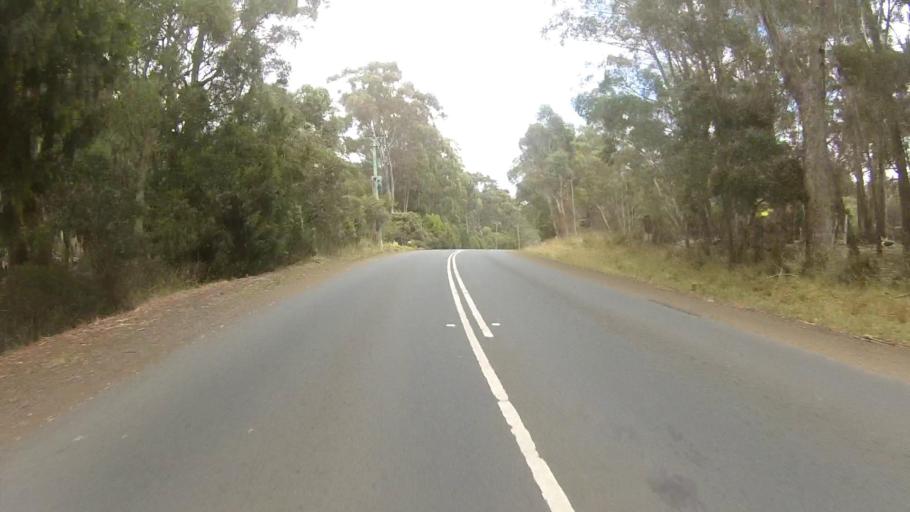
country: AU
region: Tasmania
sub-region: Kingborough
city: Margate
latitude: -42.9932
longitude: 147.2095
